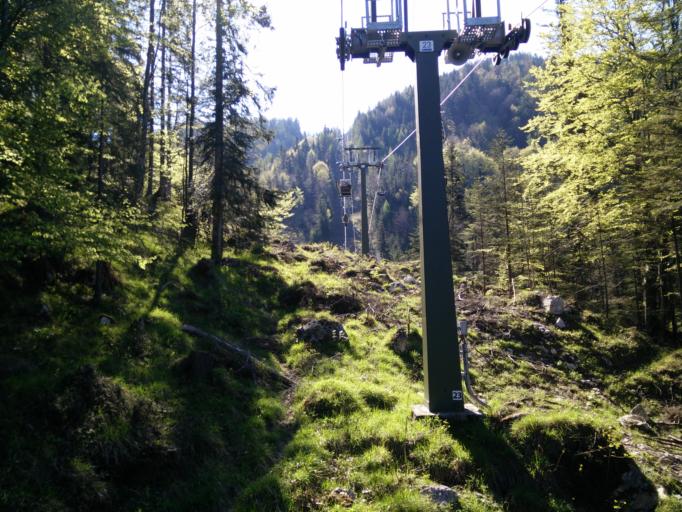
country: DE
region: Bavaria
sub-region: Upper Bavaria
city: Kiefersfelden
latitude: 47.5828
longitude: 12.2012
